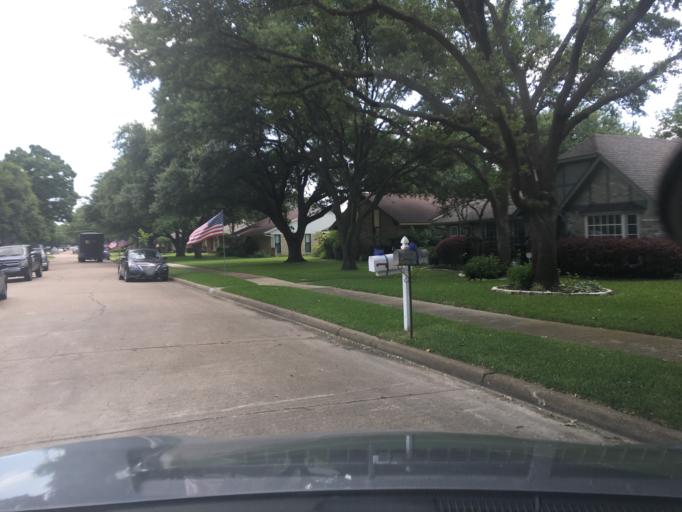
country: US
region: Texas
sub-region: Dallas County
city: Richardson
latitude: 32.9583
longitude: -96.6930
